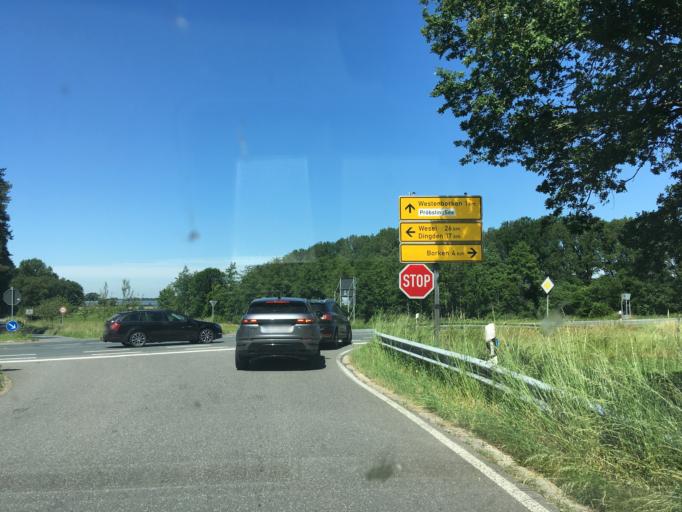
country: DE
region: North Rhine-Westphalia
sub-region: Regierungsbezirk Munster
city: Borken
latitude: 51.8164
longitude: 6.8142
